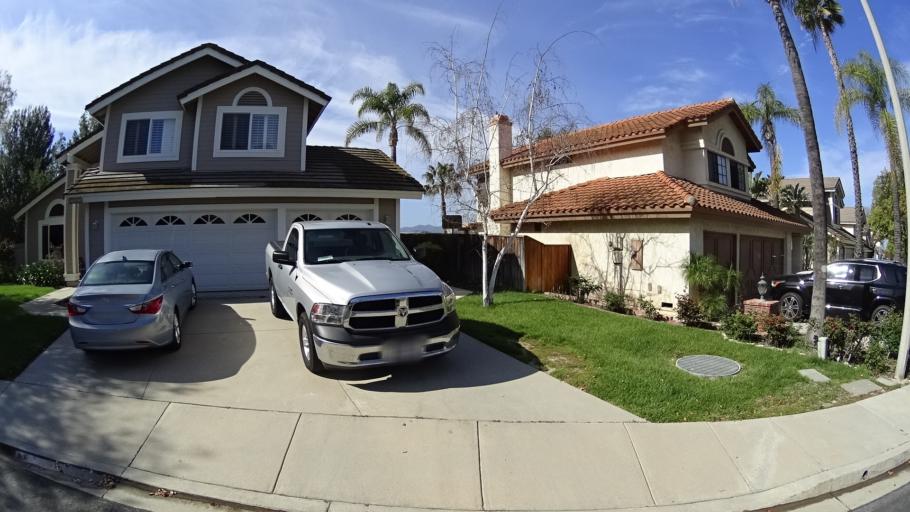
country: US
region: California
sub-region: Ventura County
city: Thousand Oaks
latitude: 34.2133
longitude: -118.8367
